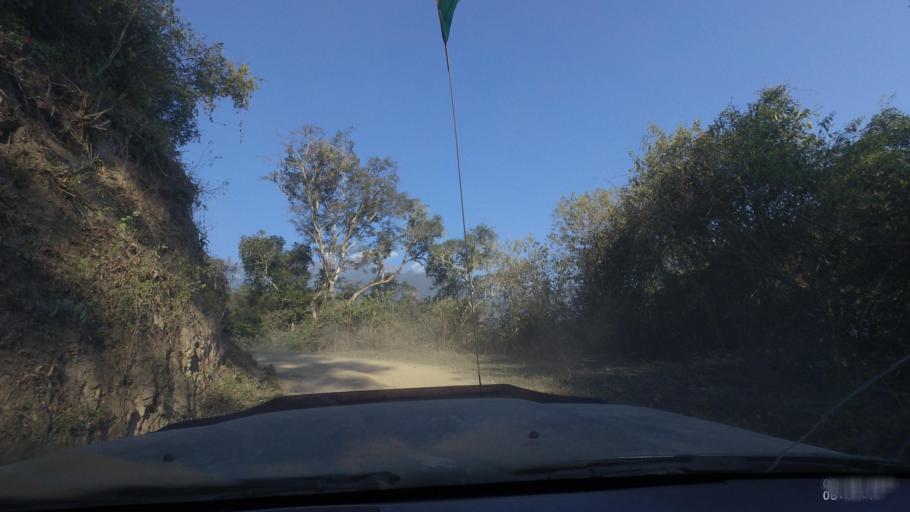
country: BO
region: La Paz
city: Quime
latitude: -16.5123
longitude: -66.7636
